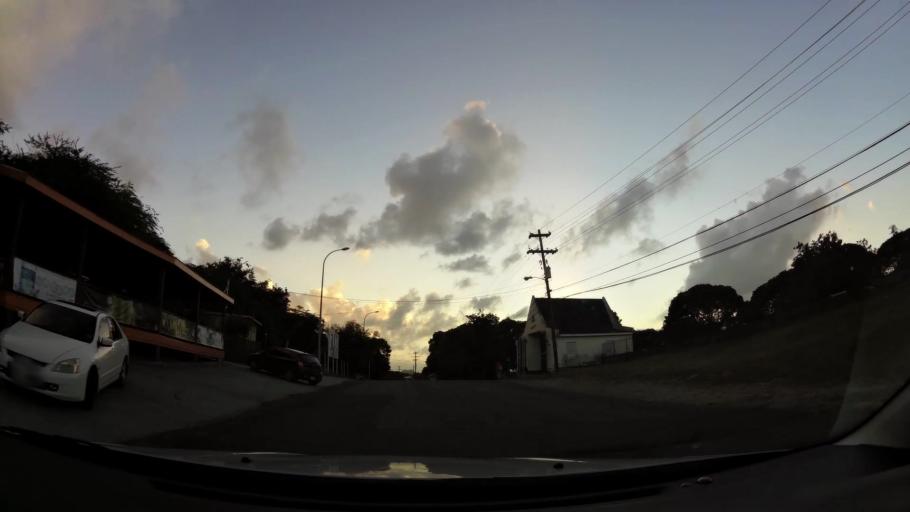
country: AG
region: Saint John
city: Saint John's
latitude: 17.1290
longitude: -61.8373
